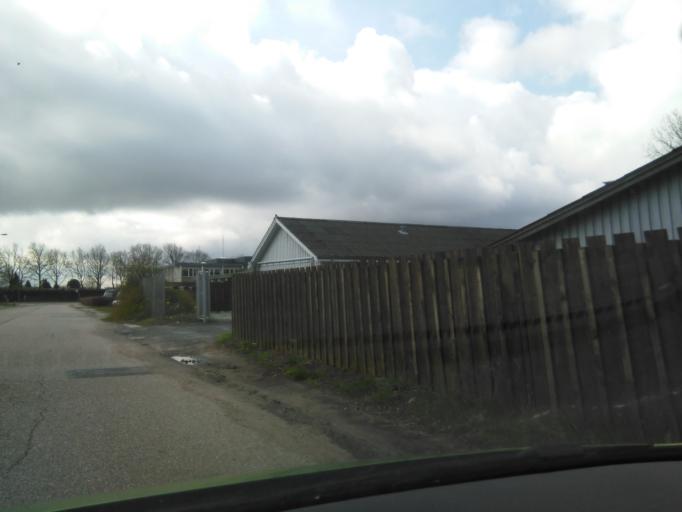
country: DK
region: Central Jutland
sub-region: Arhus Kommune
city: Stavtrup
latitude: 56.1639
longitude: 10.1249
